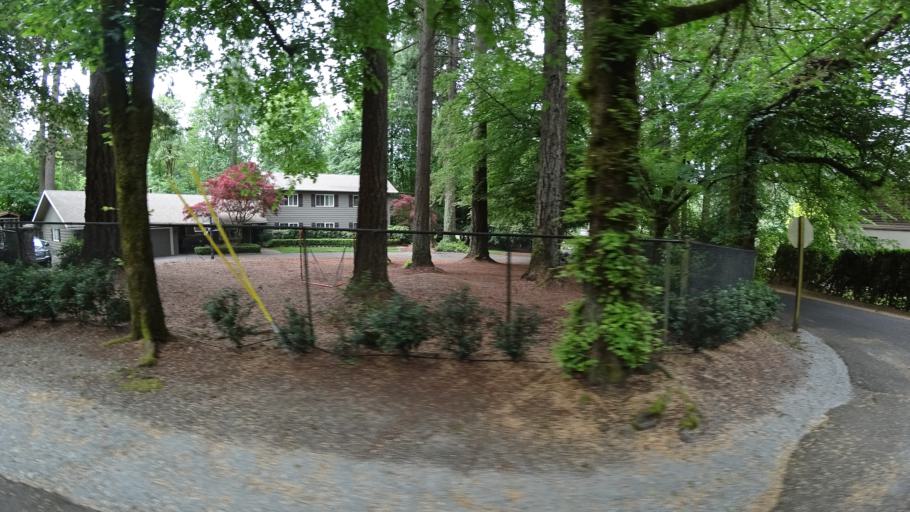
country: US
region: Oregon
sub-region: Clackamas County
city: Lake Oswego
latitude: 45.4321
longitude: -122.6636
